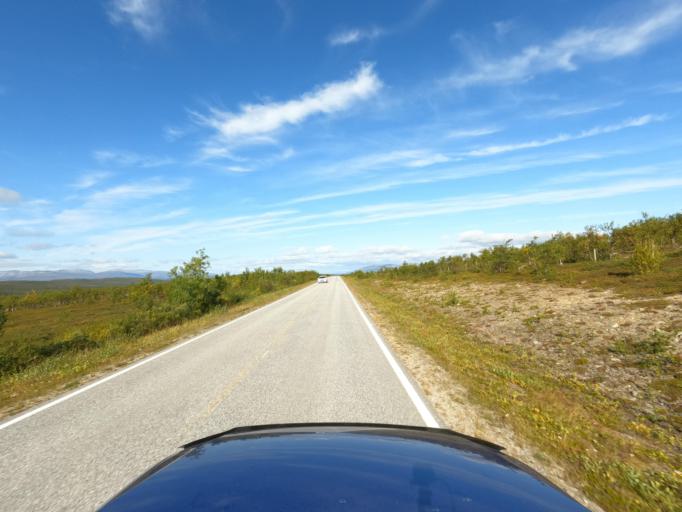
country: NO
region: Finnmark Fylke
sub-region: Karasjok
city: Karasjohka
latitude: 69.7154
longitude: 25.2399
